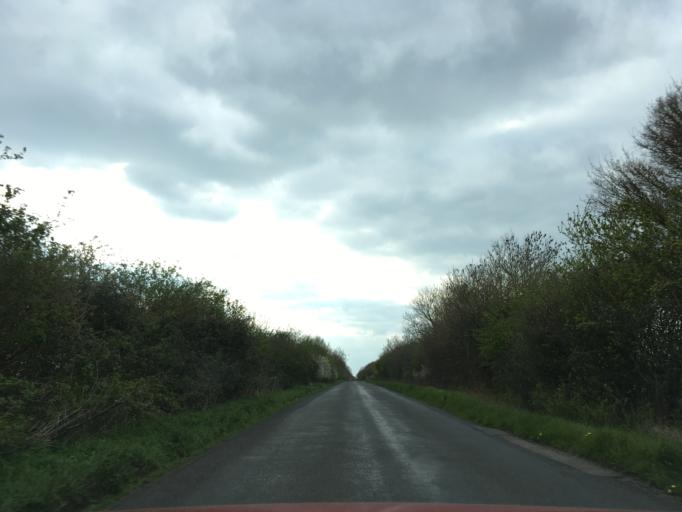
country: GB
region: England
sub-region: Oxfordshire
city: Bicester
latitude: 51.8843
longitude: -1.2189
